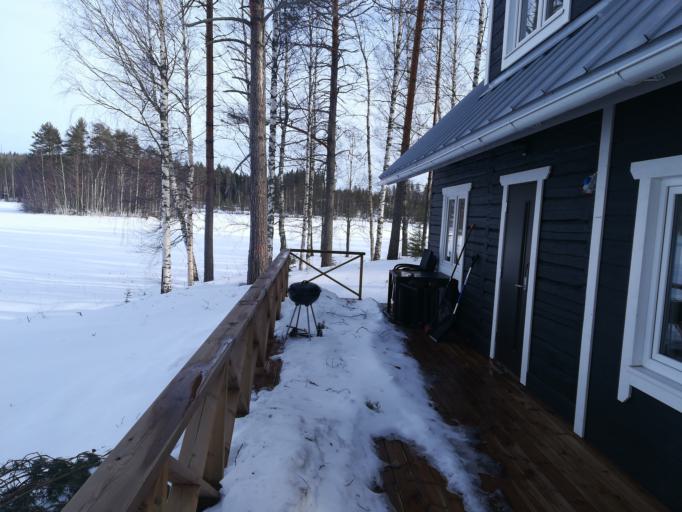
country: FI
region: Southern Savonia
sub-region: Savonlinna
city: Savonlinna
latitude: 61.8297
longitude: 29.0223
